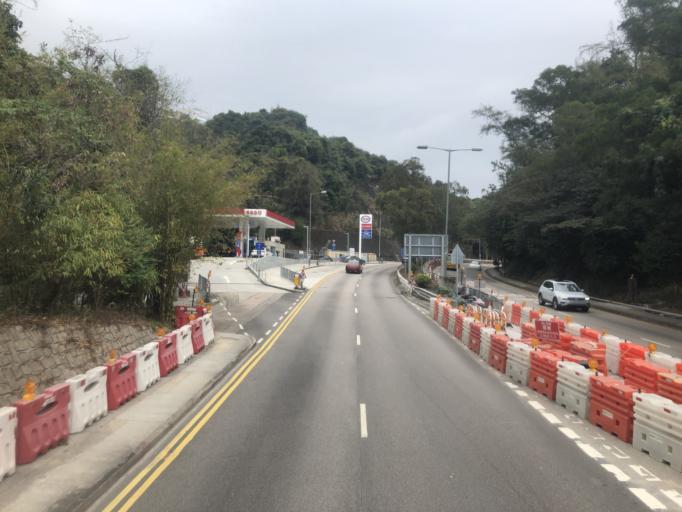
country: HK
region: Wong Tai Sin
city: Wong Tai Sin
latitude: 22.3344
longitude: 114.2290
